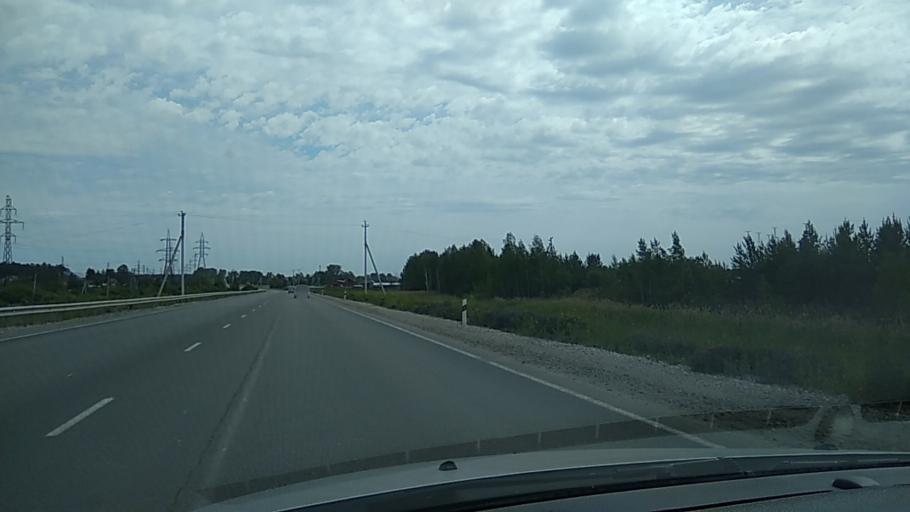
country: RU
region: Sverdlovsk
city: Verkhnyaya Pyshma
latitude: 56.9499
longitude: 60.5926
